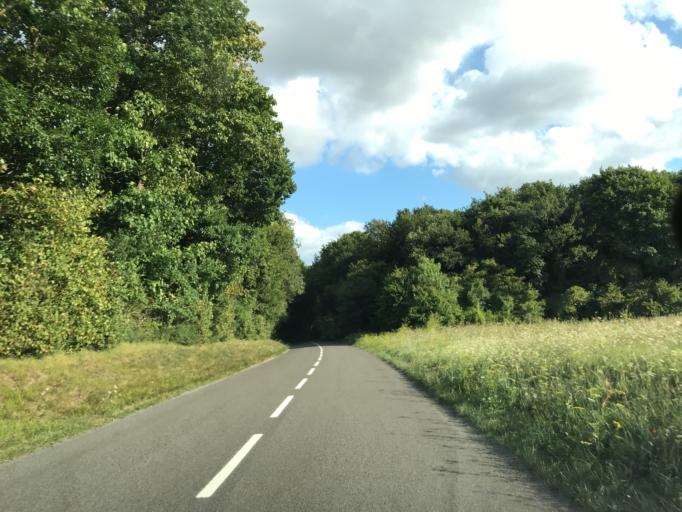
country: FR
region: Haute-Normandie
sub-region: Departement de l'Eure
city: Courcelles-sur-Seine
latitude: 49.1832
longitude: 1.3858
